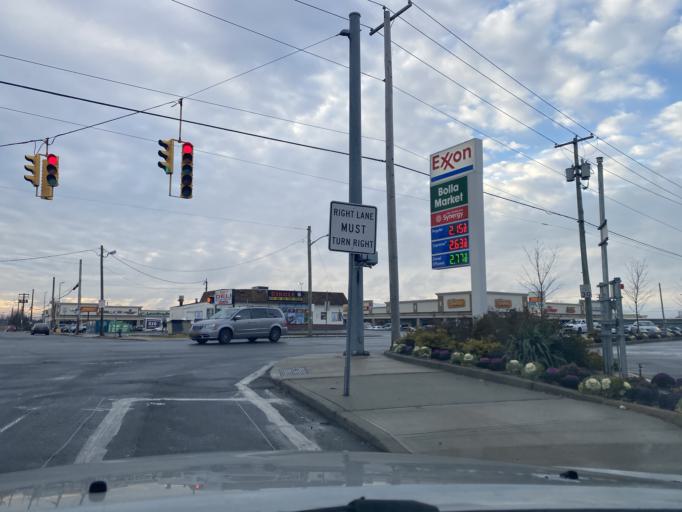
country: US
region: New York
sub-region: Nassau County
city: Lawrence
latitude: 40.6243
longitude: -73.7350
